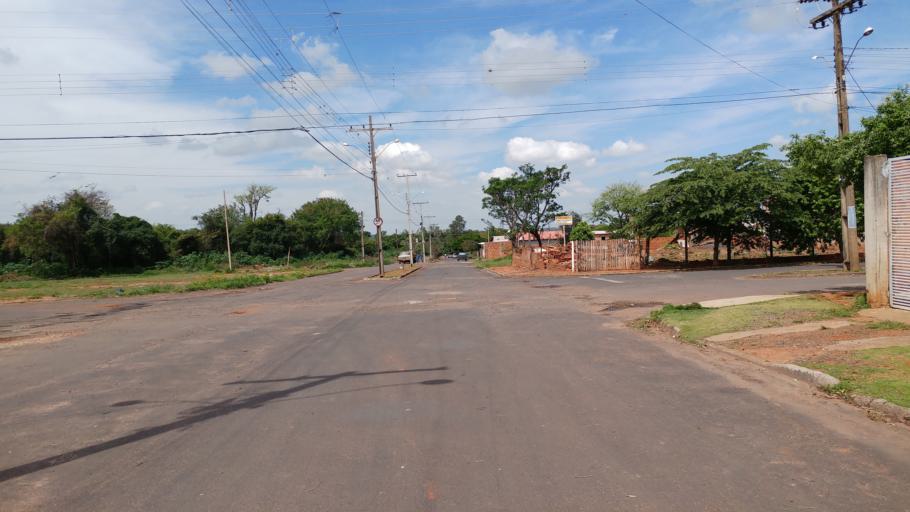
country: BR
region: Sao Paulo
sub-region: Paraguacu Paulista
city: Paraguacu Paulista
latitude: -22.4325
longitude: -50.5755
